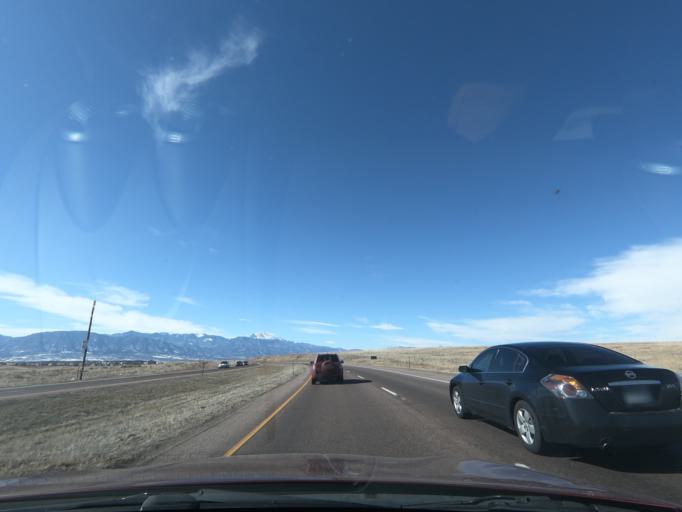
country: US
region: Colorado
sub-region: El Paso County
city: Security-Widefield
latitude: 38.7654
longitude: -104.6867
